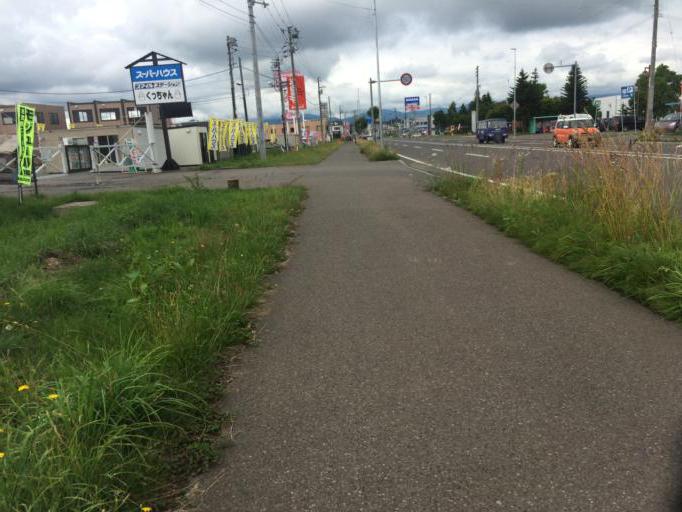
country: JP
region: Hokkaido
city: Niseko Town
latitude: 42.8875
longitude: 140.7512
